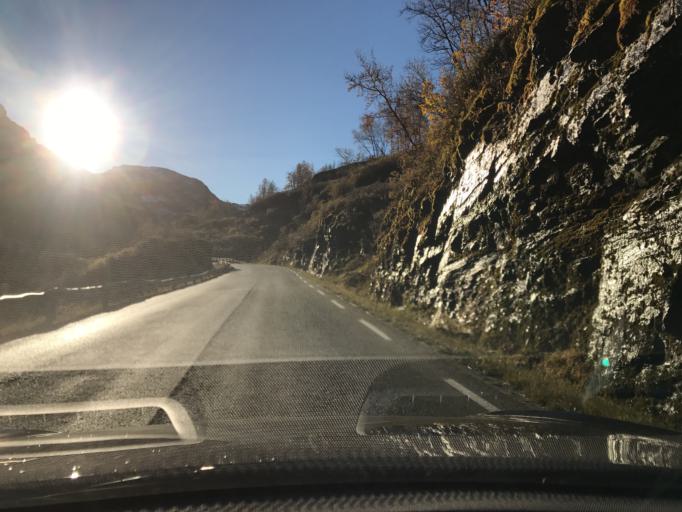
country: NO
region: Sogn og Fjordane
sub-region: Laerdal
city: Laerdalsoyri
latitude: 60.8150
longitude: 7.5505
